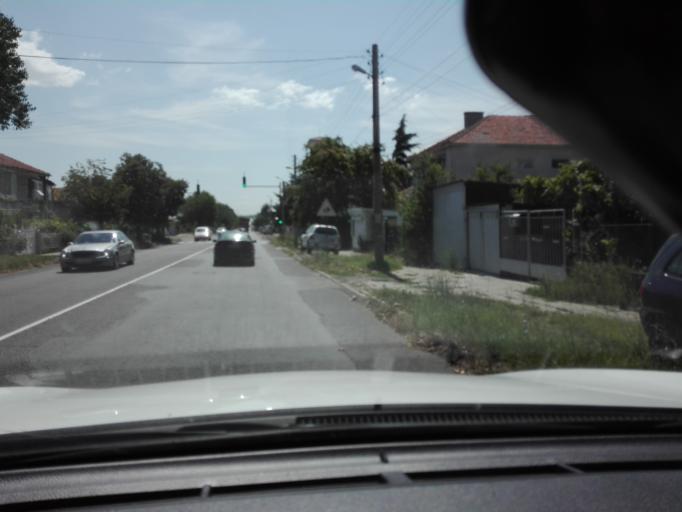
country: BG
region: Burgas
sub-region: Obshtina Kameno
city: Kameno
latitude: 42.6015
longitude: 27.3870
